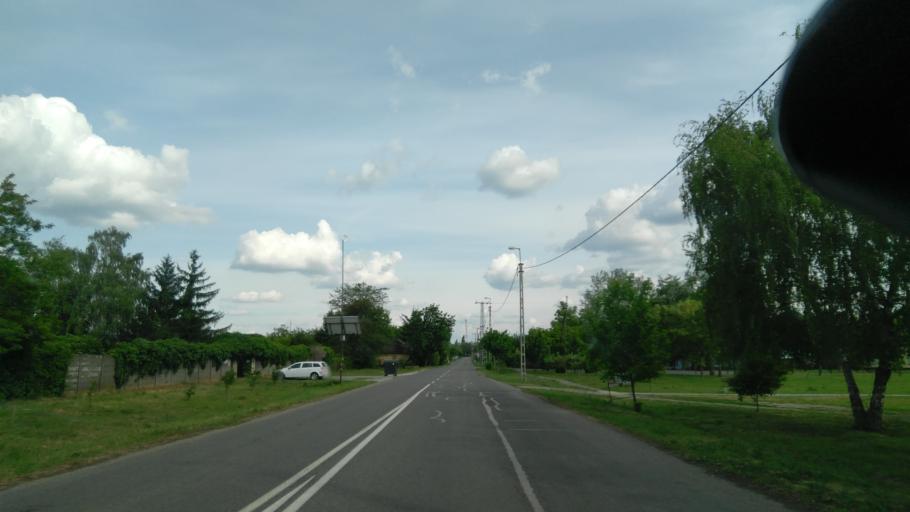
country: HU
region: Bekes
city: Battonya
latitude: 46.2856
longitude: 21.0360
